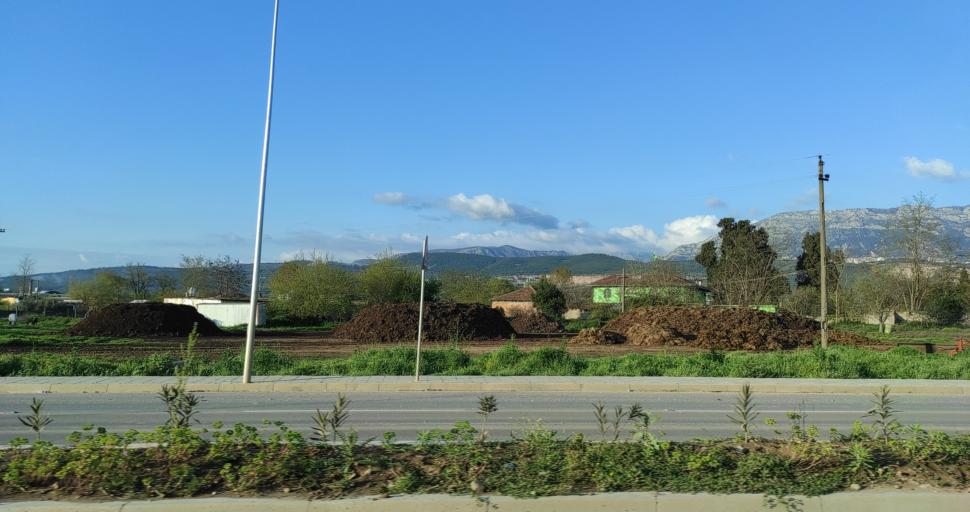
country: AL
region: Durres
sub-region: Rrethi i Krujes
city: Fushe-Kruje
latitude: 41.4864
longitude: 19.7276
